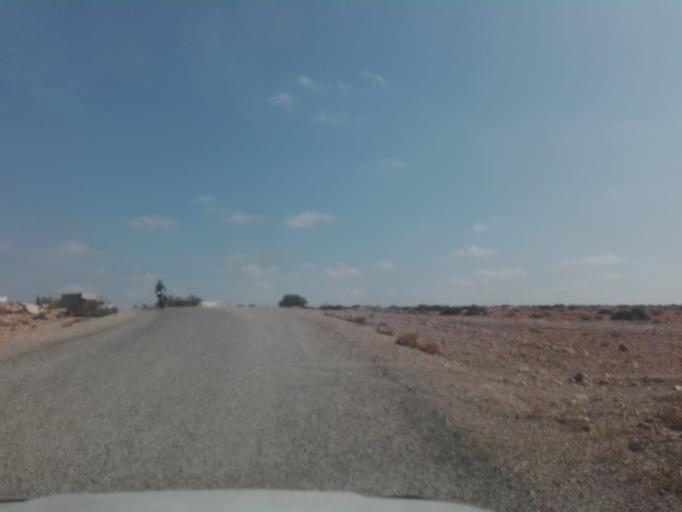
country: TN
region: Madanin
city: Medenine
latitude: 33.4394
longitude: 10.4324
